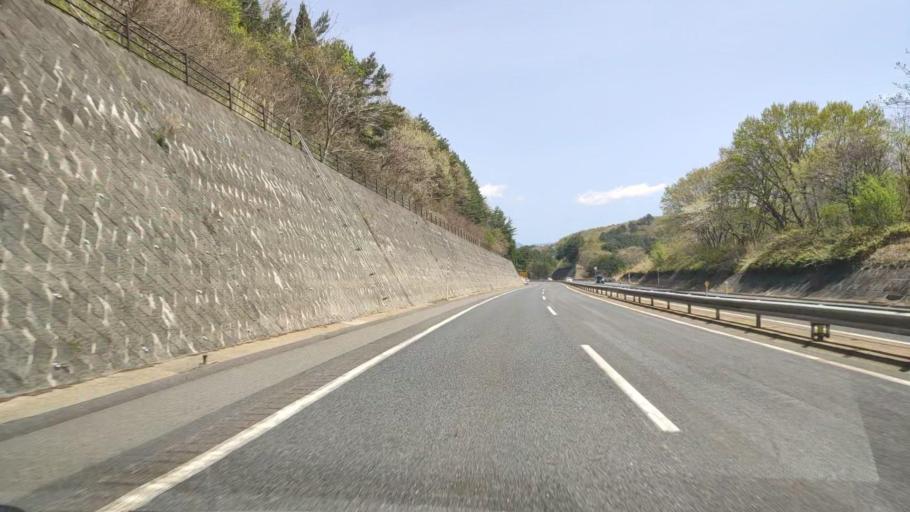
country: JP
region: Iwate
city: Ichinohe
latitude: 40.3058
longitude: 141.4259
